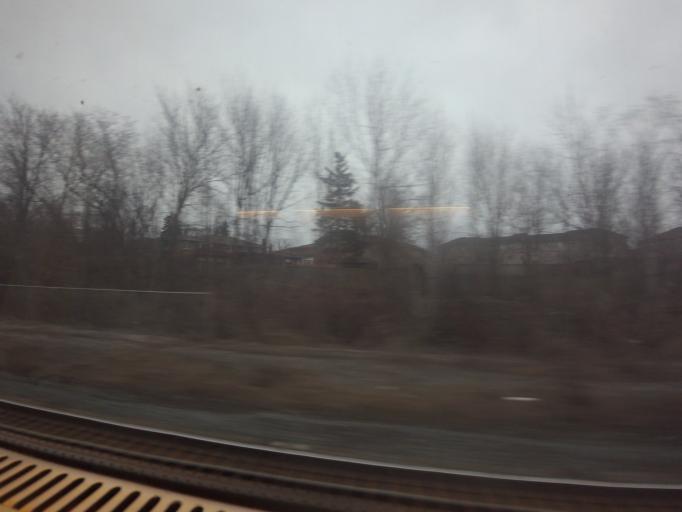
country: CA
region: Ontario
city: Scarborough
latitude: 43.7451
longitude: -79.2242
